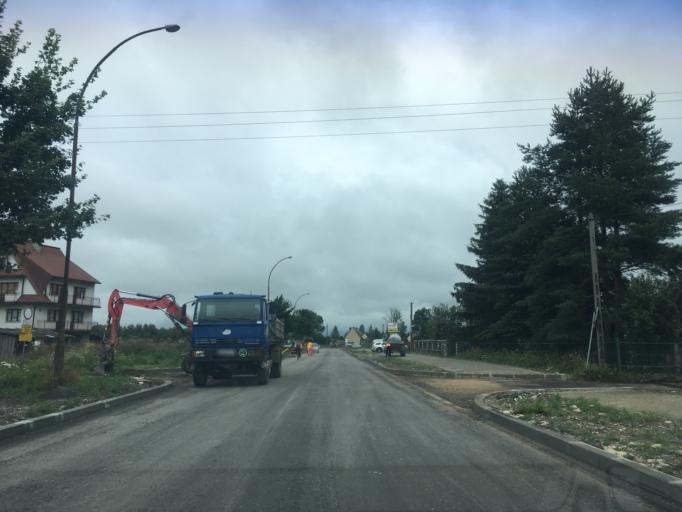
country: PL
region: Lesser Poland Voivodeship
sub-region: Powiat nowotarski
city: Czarny Dunajec
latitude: 49.4446
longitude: 19.8564
